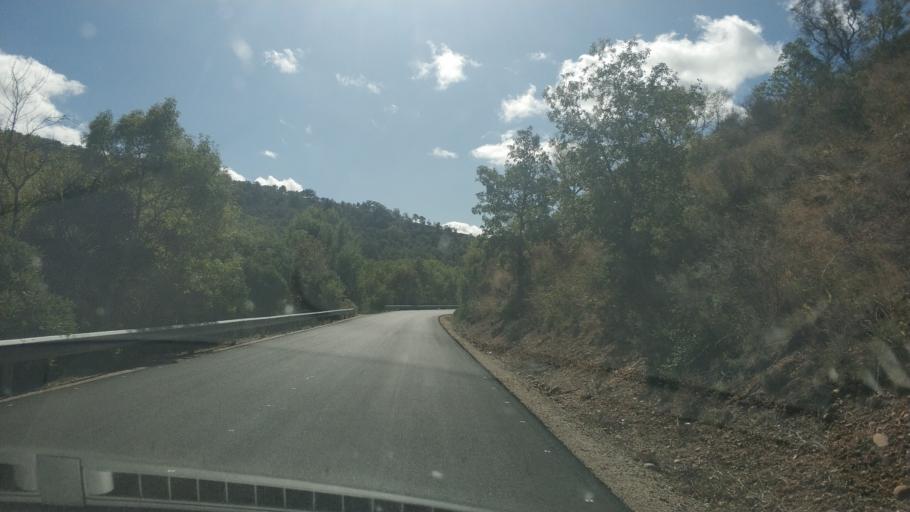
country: ES
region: Castille and Leon
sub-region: Provincia de Burgos
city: Covarrubias
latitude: 42.0524
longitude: -3.5234
